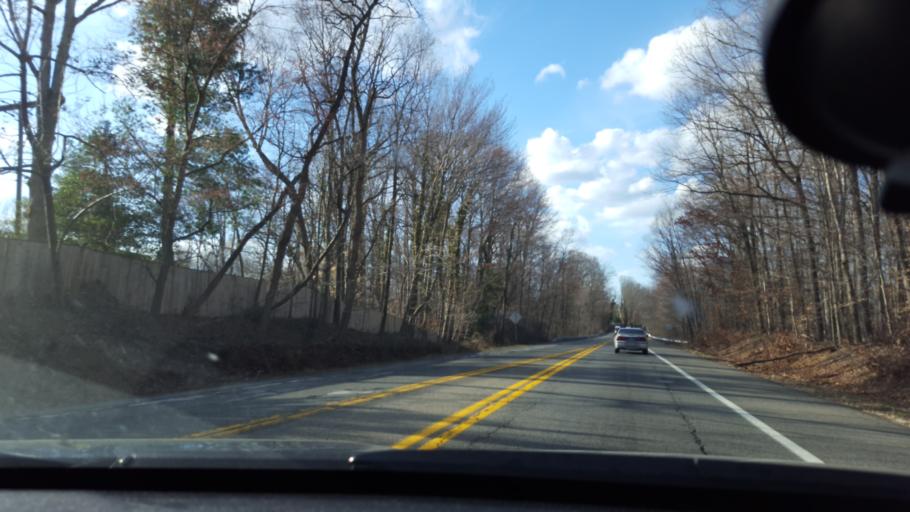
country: US
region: Maryland
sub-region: Prince George's County
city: Bowie
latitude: 38.9598
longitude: -76.7489
